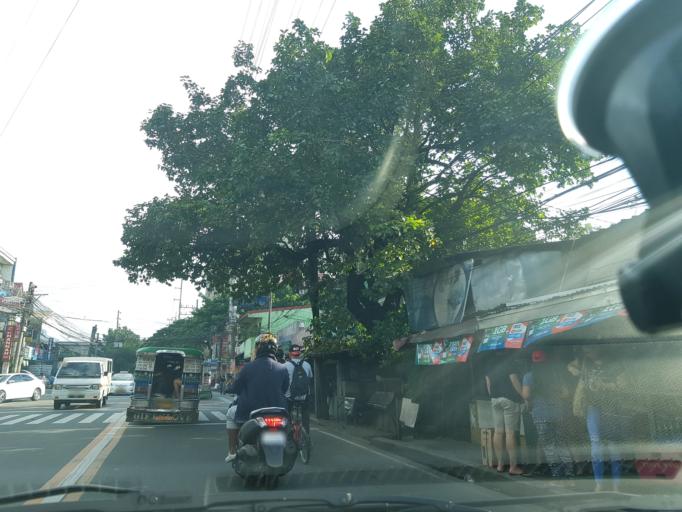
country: PH
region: Metro Manila
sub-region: Marikina
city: Calumpang
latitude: 14.6070
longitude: 121.0923
